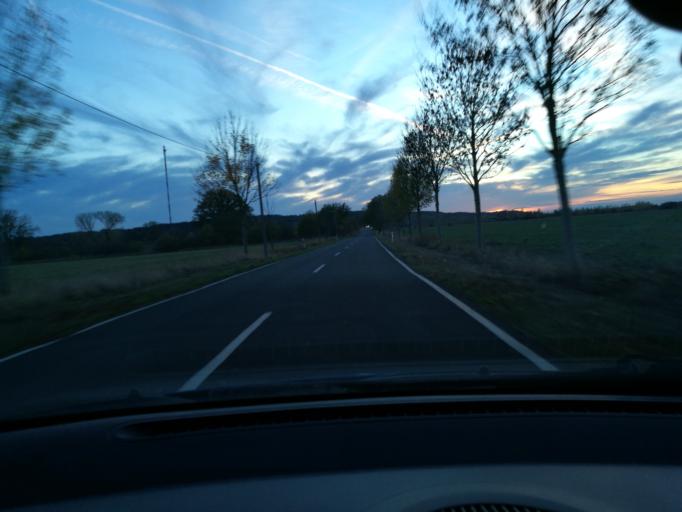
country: DE
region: Brandenburg
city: Lenzen
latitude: 53.0826
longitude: 11.4610
